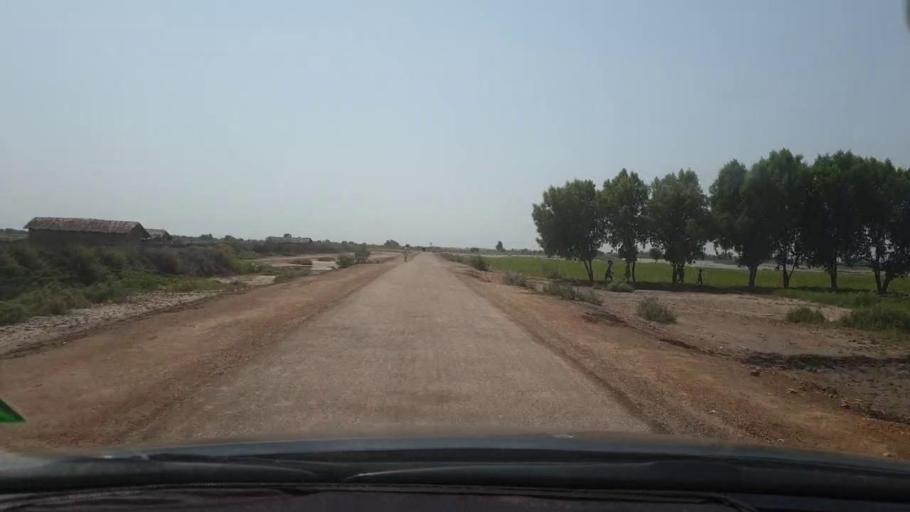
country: PK
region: Sindh
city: Tando Bago
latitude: 24.7974
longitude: 69.1680
